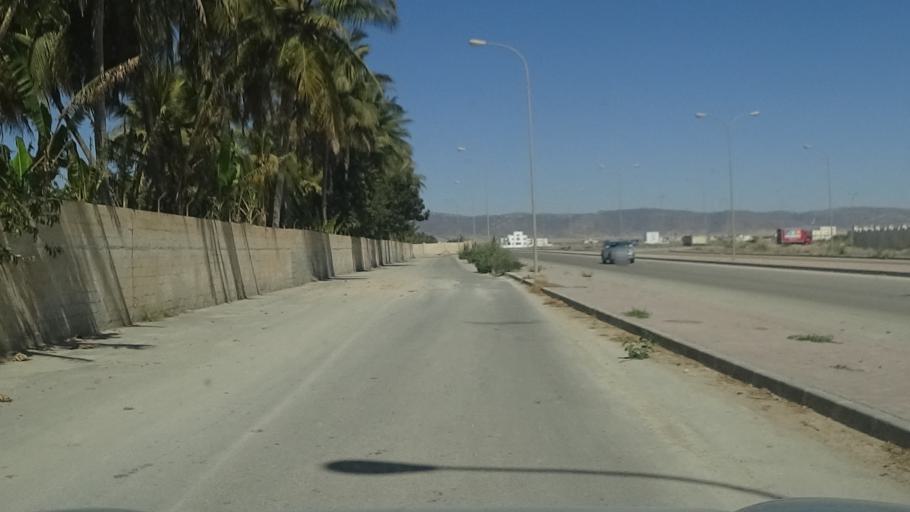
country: OM
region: Zufar
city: Salalah
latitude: 17.0286
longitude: 54.1231
